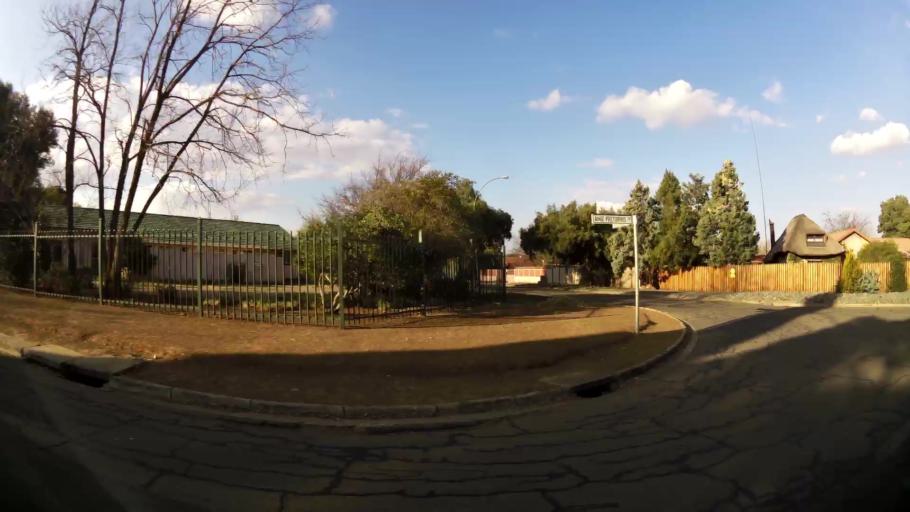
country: ZA
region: Orange Free State
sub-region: Mangaung Metropolitan Municipality
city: Bloemfontein
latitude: -29.1614
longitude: 26.1802
